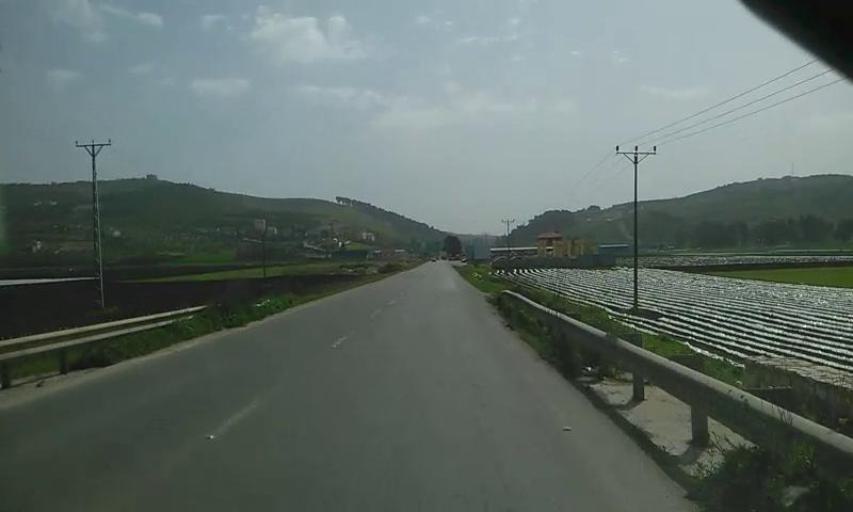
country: PS
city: Bir al Basha
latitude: 32.4135
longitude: 35.2285
